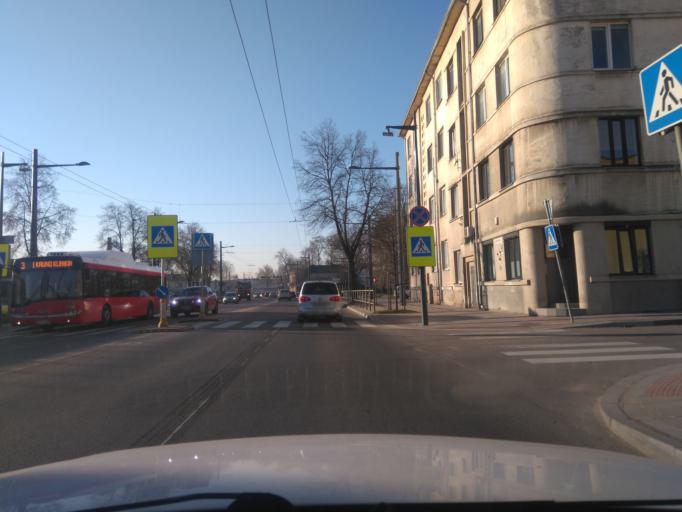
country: LT
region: Kauno apskritis
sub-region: Kaunas
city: Aleksotas
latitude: 54.8772
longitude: 23.9345
